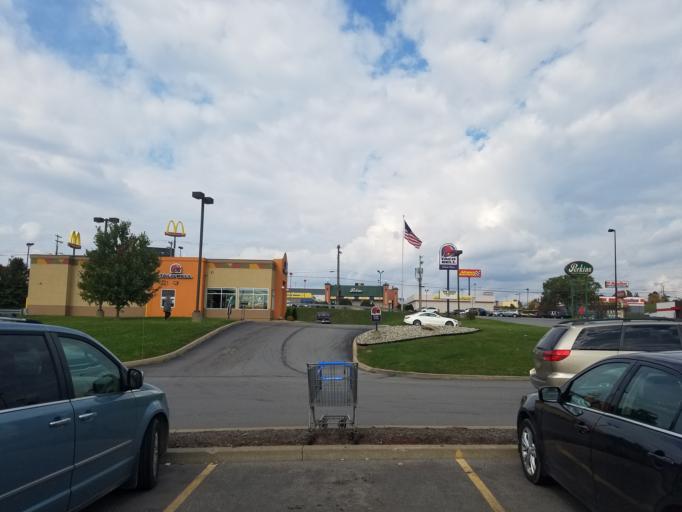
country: US
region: Pennsylvania
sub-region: Clarion County
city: Clarion
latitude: 41.1895
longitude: -79.3953
